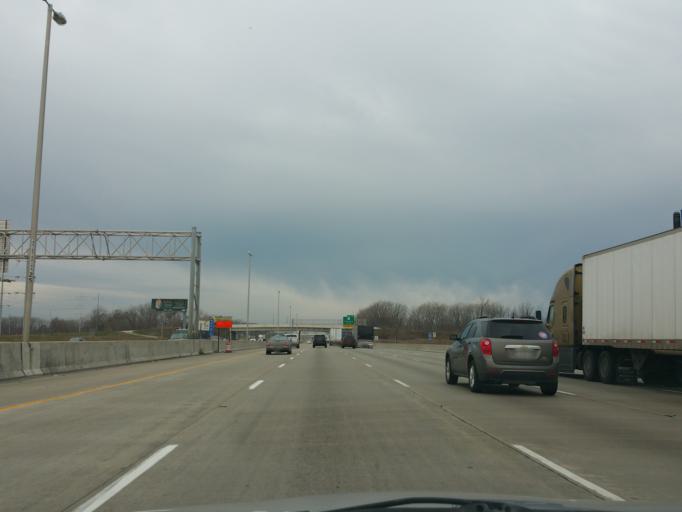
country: US
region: Indiana
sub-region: Lake County
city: Gary
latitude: 41.5675
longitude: -87.3224
